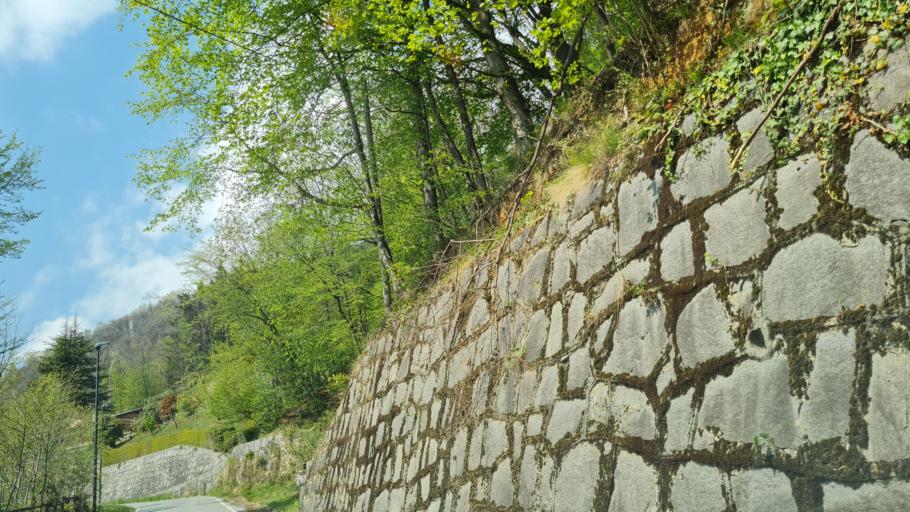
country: IT
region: Piedmont
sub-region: Provincia di Biella
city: Sordevolo
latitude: 45.5785
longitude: 7.9689
